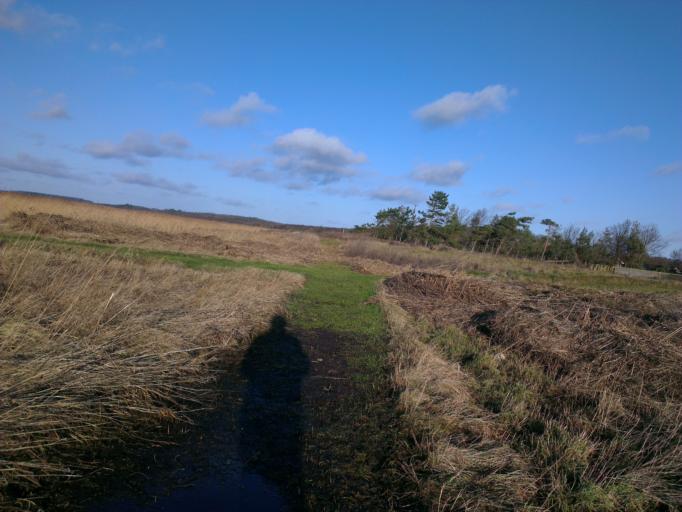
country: DK
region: Capital Region
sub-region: Frederikssund Kommune
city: Jaegerspris
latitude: 55.8410
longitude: 11.9567
